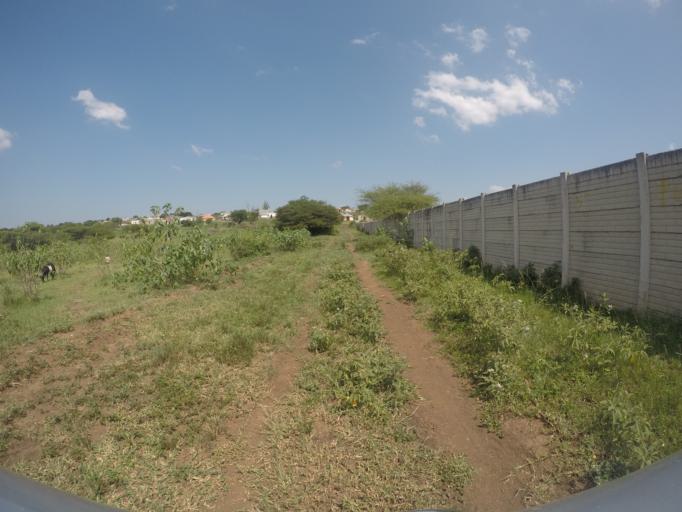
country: ZA
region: KwaZulu-Natal
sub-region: uThungulu District Municipality
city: Empangeni
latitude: -28.5867
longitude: 31.7423
